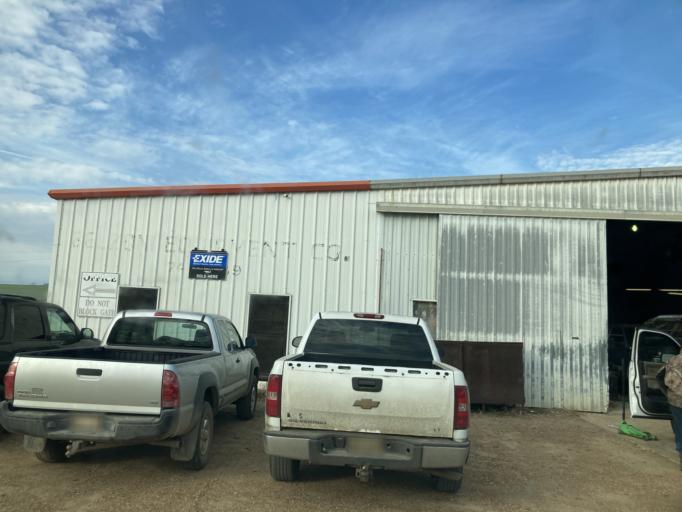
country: US
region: Mississippi
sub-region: Humphreys County
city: Belzoni
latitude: 33.1678
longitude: -90.4972
